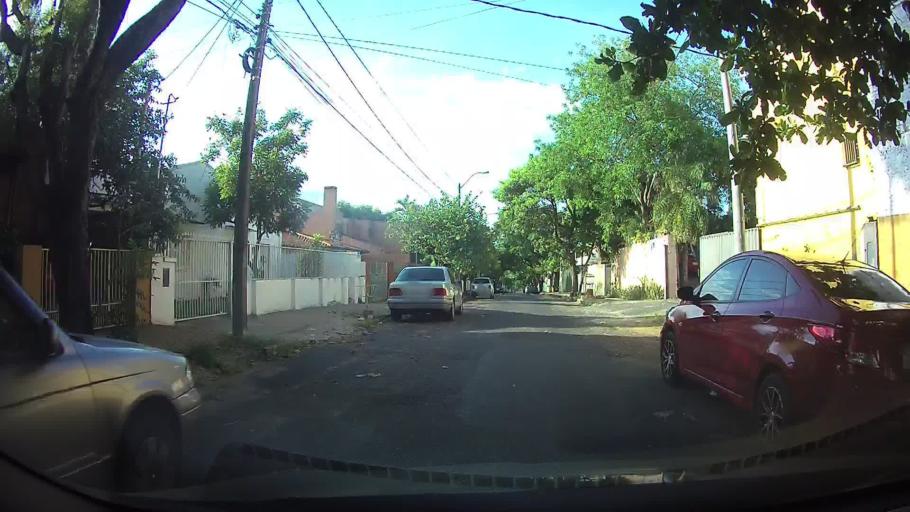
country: PY
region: Asuncion
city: Asuncion
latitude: -25.2862
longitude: -57.6033
